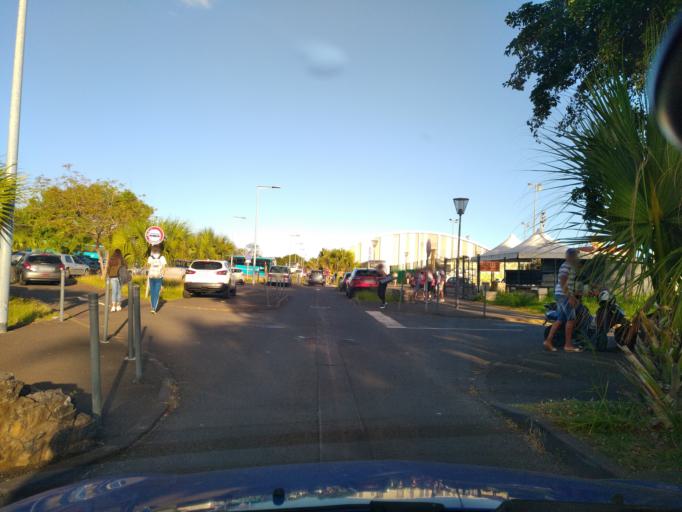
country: RE
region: Reunion
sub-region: Reunion
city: Saint-Pierre
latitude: -21.3427
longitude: 55.4909
